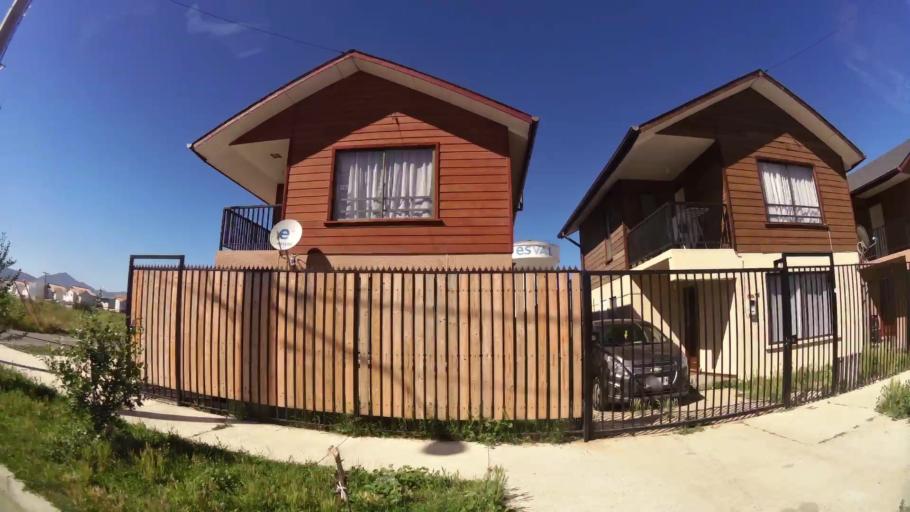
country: CL
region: Valparaiso
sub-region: Provincia de Marga Marga
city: Quilpue
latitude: -33.3239
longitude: -71.3969
